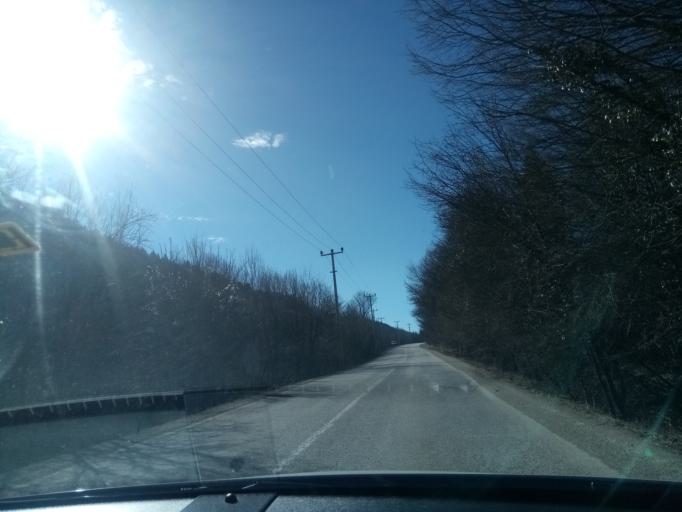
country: TR
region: Duzce
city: Kaynasli
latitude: 40.6575
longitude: 31.3937
